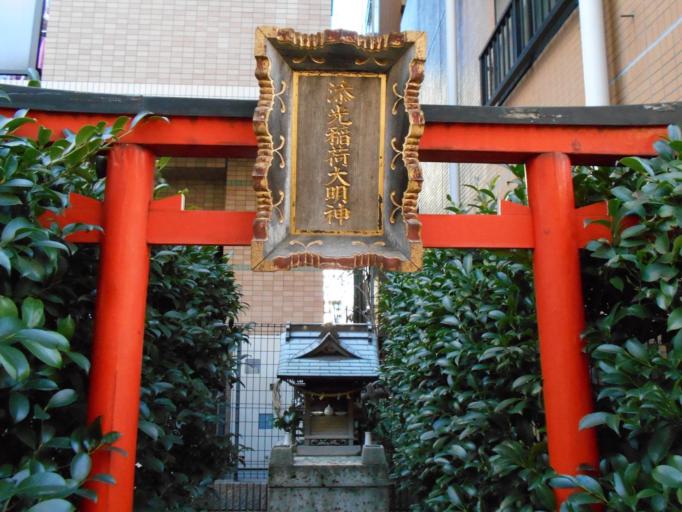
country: JP
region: Tokyo
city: Urayasu
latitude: 35.7082
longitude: 139.8054
